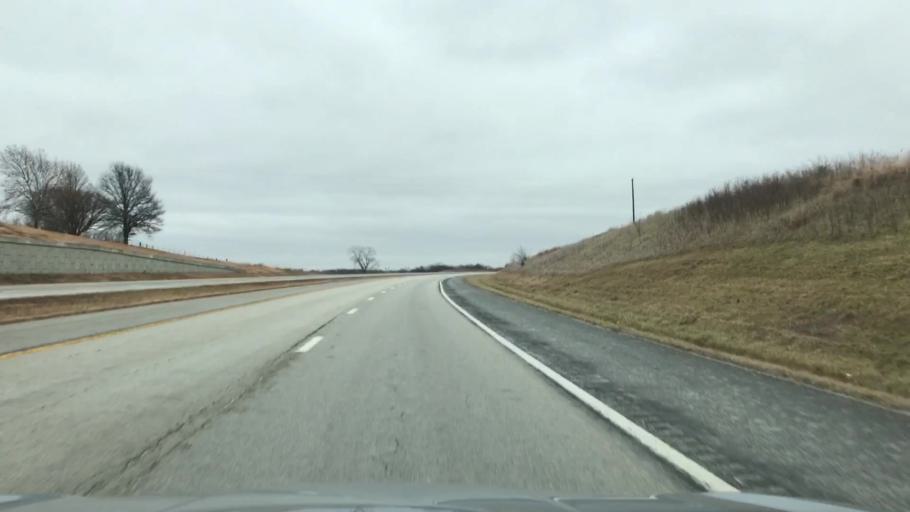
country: US
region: Missouri
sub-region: Caldwell County
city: Hamilton
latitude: 39.7487
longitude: -94.0548
